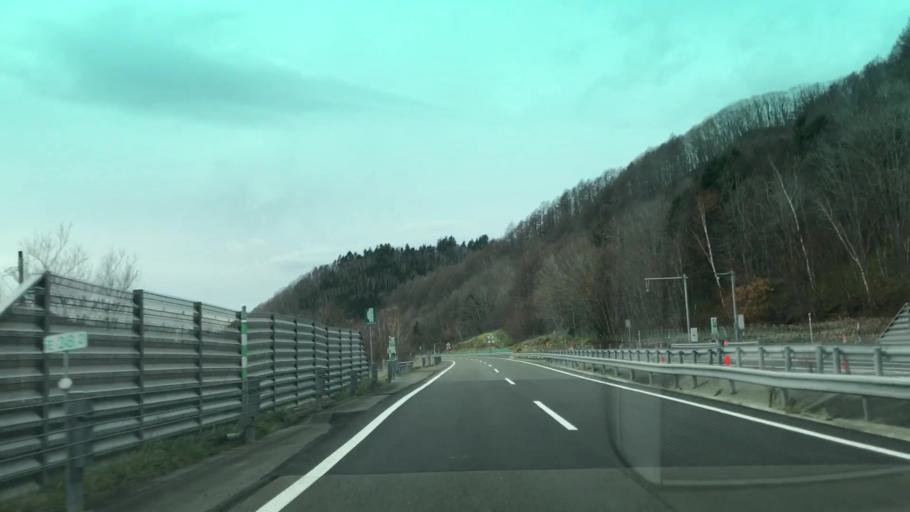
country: JP
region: Hokkaido
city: Chitose
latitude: 42.9063
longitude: 141.9998
